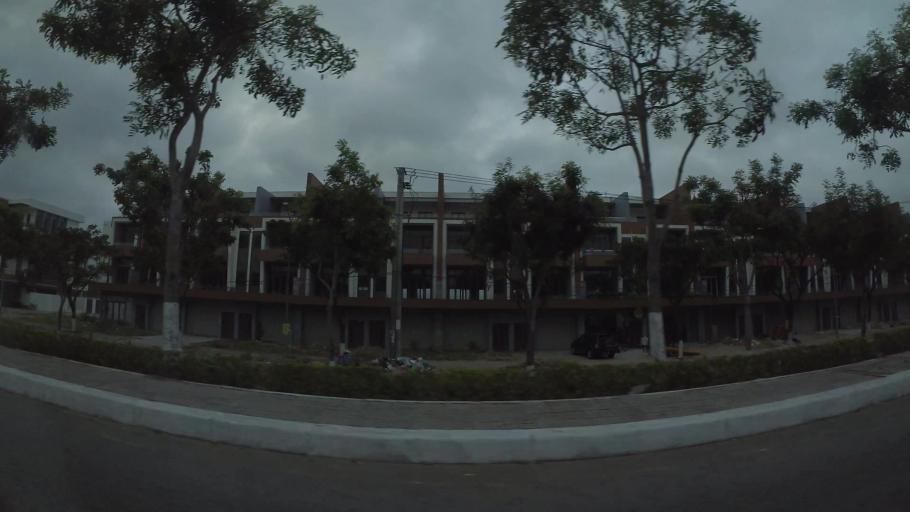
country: VN
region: Da Nang
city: Son Tra
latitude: 16.0345
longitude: 108.2313
